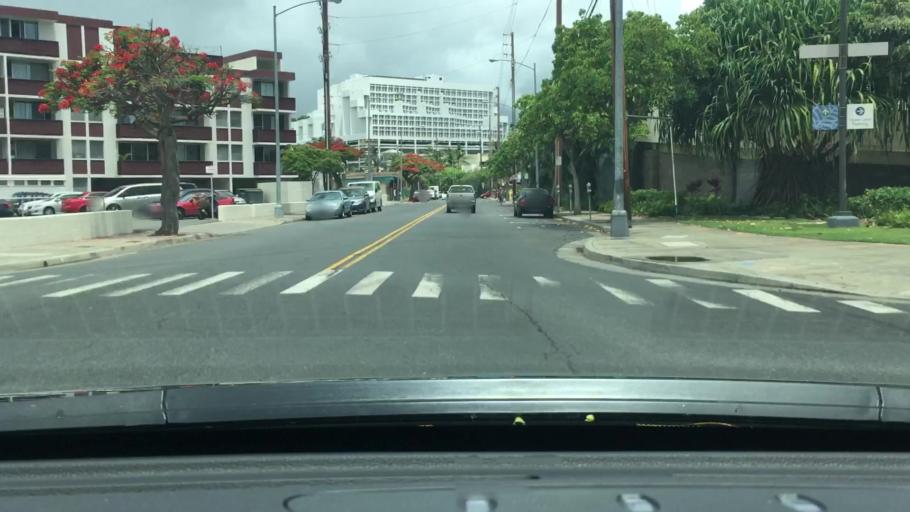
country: US
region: Hawaii
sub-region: Honolulu County
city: Honolulu
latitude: 21.2951
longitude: -157.8445
